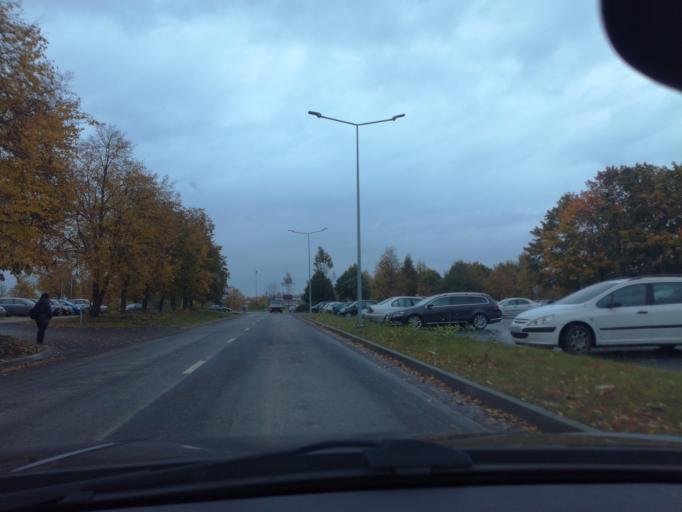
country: LT
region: Alytaus apskritis
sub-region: Alytus
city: Alytus
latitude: 54.4191
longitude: 24.0205
